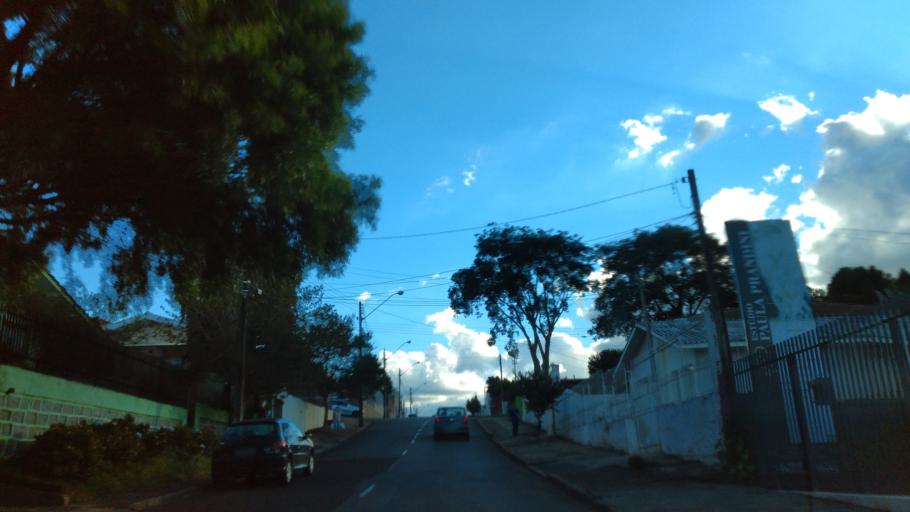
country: BR
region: Parana
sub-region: Guarapuava
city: Guarapuava
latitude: -25.3853
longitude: -51.4606
